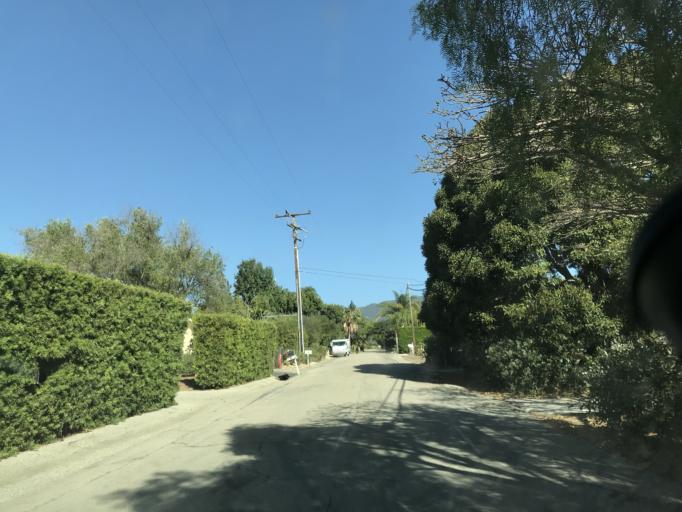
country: US
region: California
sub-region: Santa Barbara County
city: Goleta
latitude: 34.4533
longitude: -119.7861
